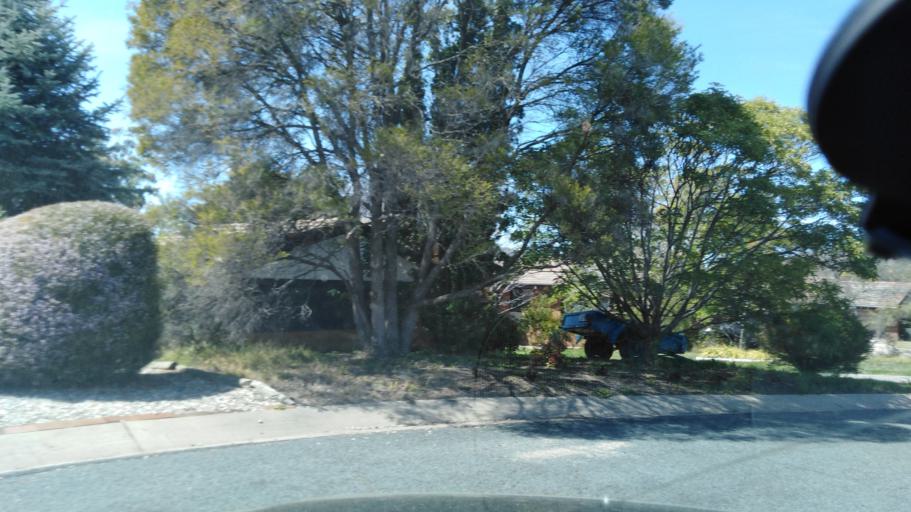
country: AU
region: Australian Capital Territory
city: Forrest
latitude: -35.3492
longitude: 149.0346
